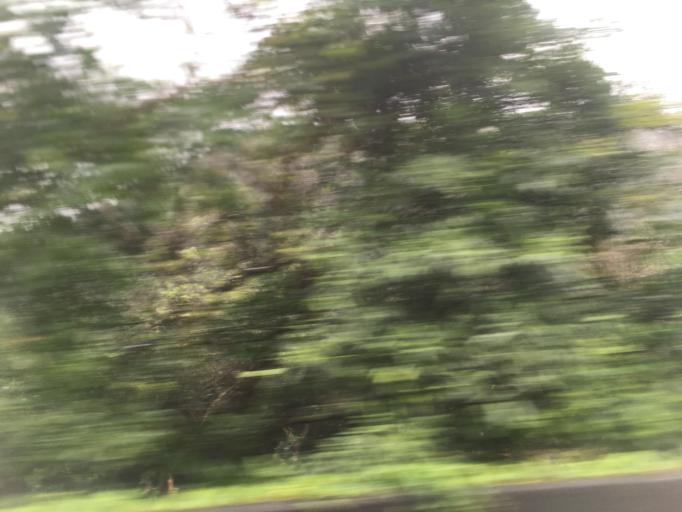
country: TW
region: Taiwan
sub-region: Keelung
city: Keelung
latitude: 25.0724
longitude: 121.9086
